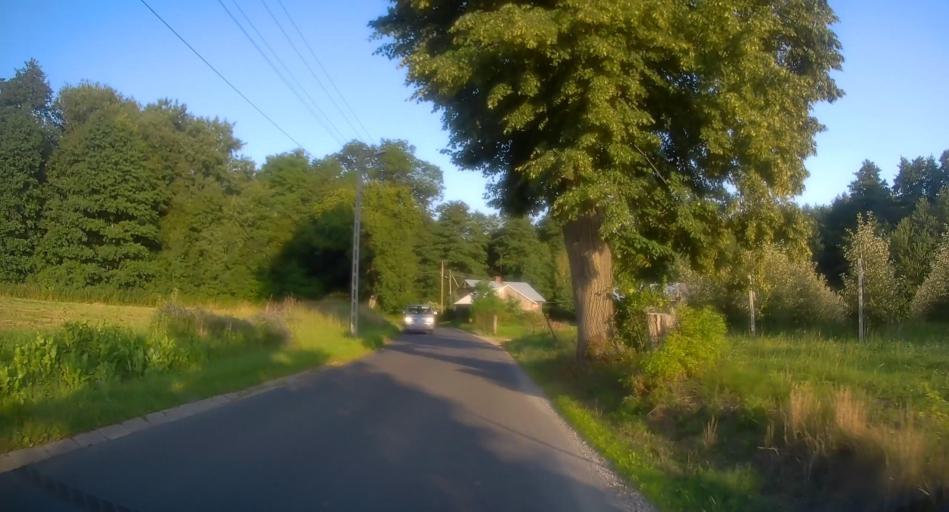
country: PL
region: Lodz Voivodeship
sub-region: Powiat skierniewicki
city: Kowiesy
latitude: 51.8887
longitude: 20.4125
